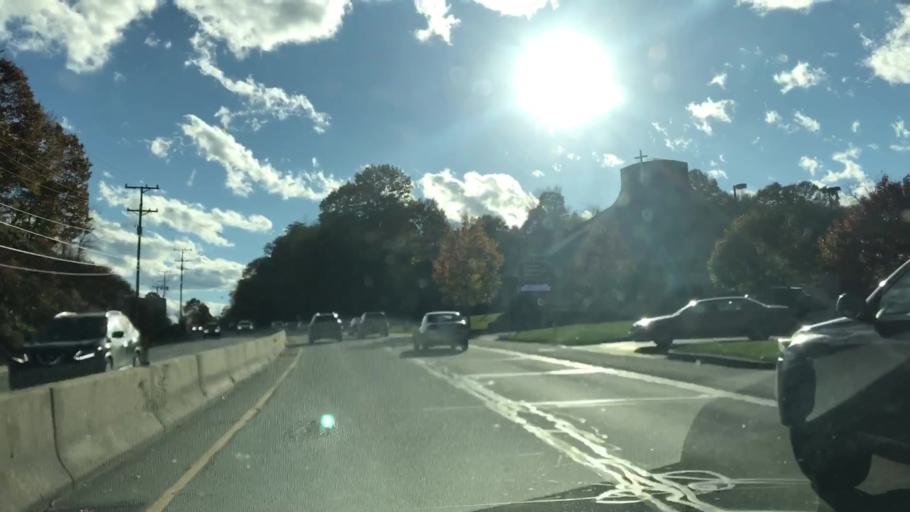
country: US
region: Pennsylvania
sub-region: Allegheny County
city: West View
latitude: 40.5042
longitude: -80.0099
